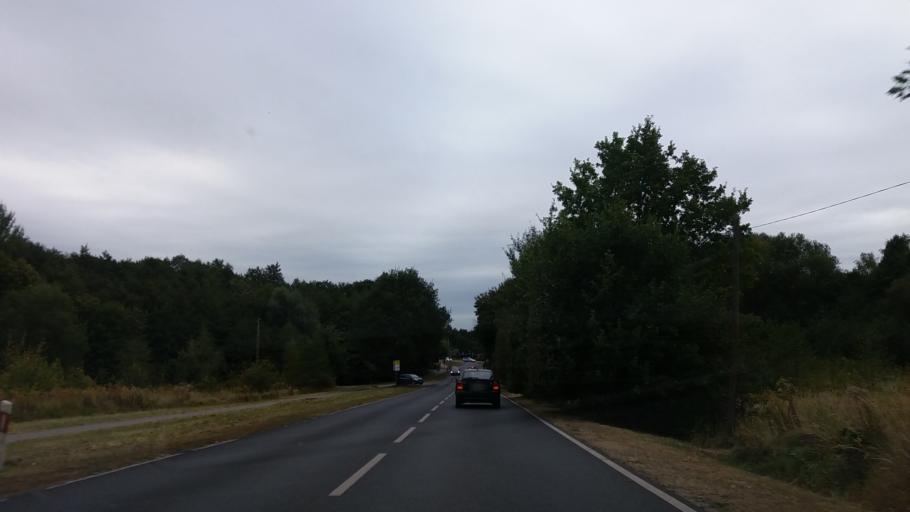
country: PL
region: Lubusz
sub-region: Powiat gorzowski
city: Klodawa
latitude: 52.7639
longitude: 15.2300
